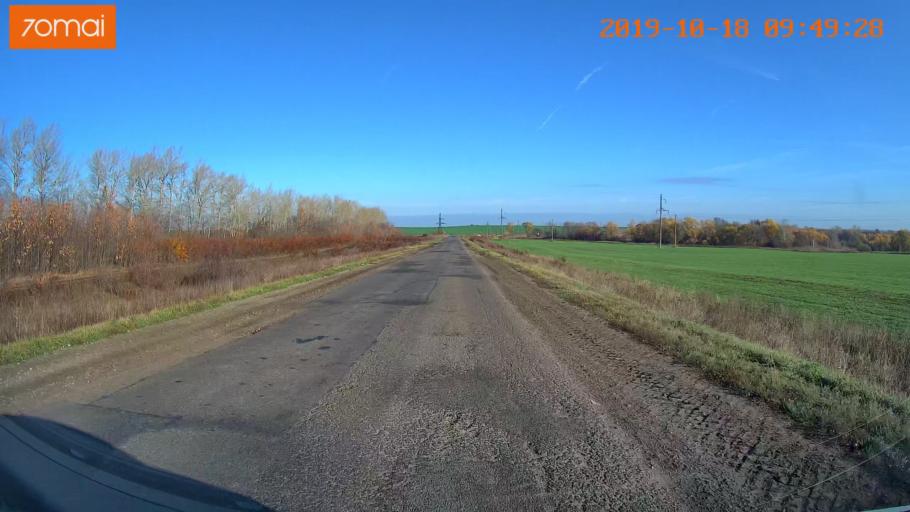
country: RU
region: Tula
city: Kazachka
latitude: 53.3183
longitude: 38.2680
